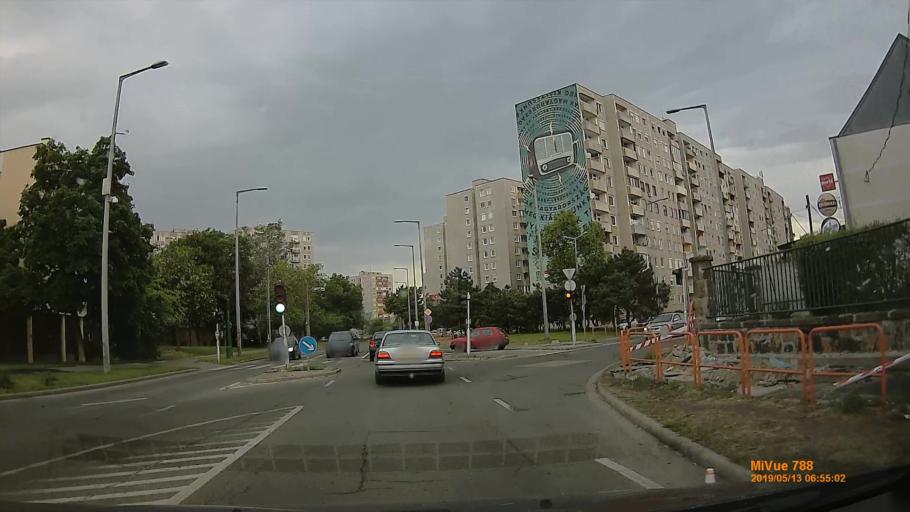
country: HU
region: Budapest
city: Budapest XXI. keruelet
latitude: 47.4209
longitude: 19.0719
